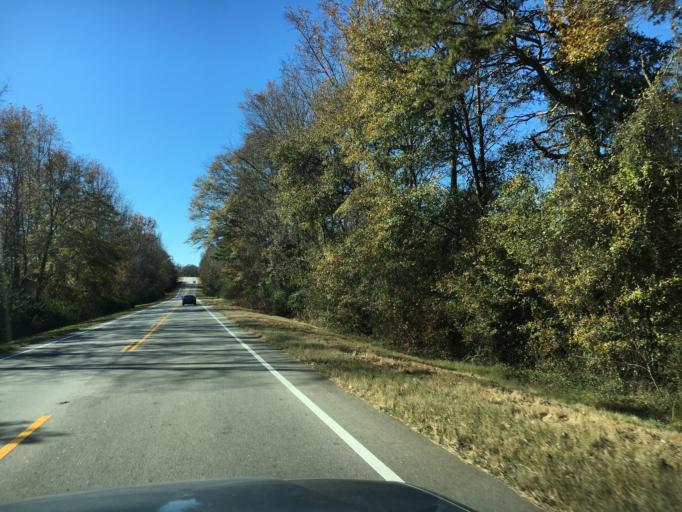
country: US
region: Georgia
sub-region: Hart County
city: Royston
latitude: 34.2940
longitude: -83.0160
